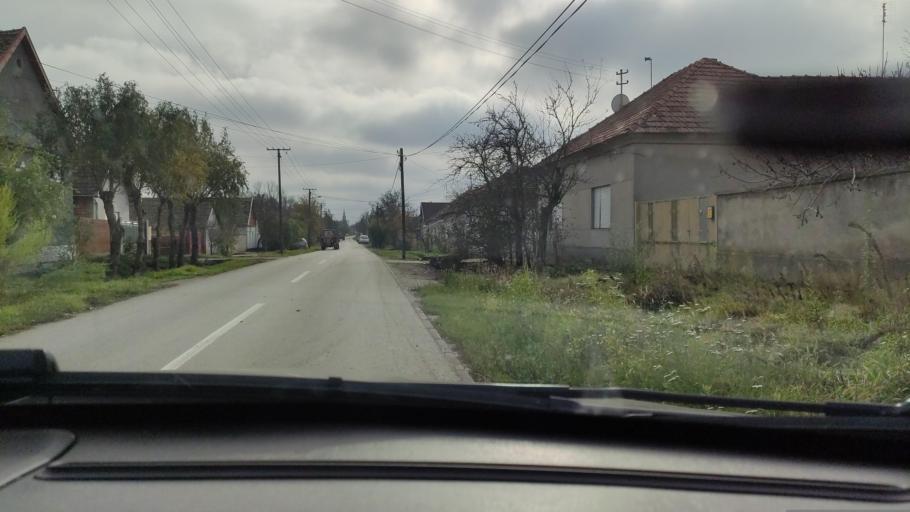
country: RS
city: Jazovo
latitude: 45.9021
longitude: 20.2167
